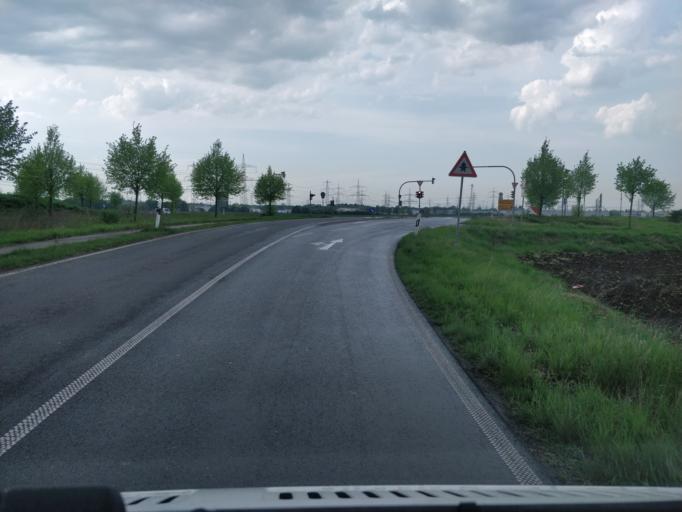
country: DE
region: North Rhine-Westphalia
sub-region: Regierungsbezirk Koln
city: Frechen
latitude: 50.9521
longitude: 6.8162
